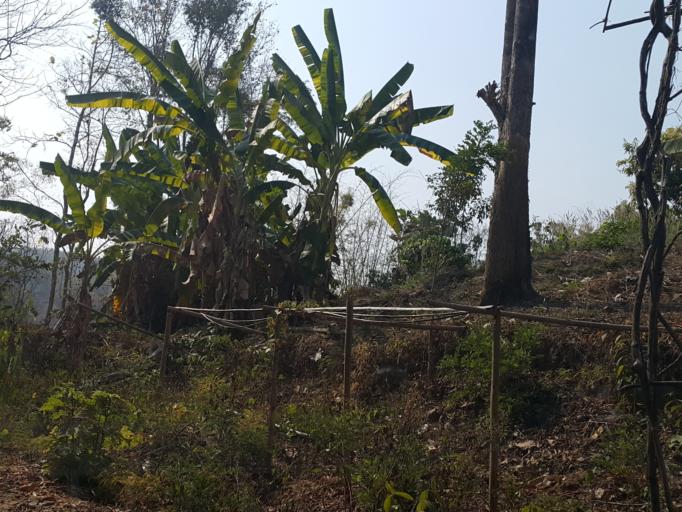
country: TH
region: Chiang Mai
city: Hang Dong
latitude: 18.7349
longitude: 98.8605
